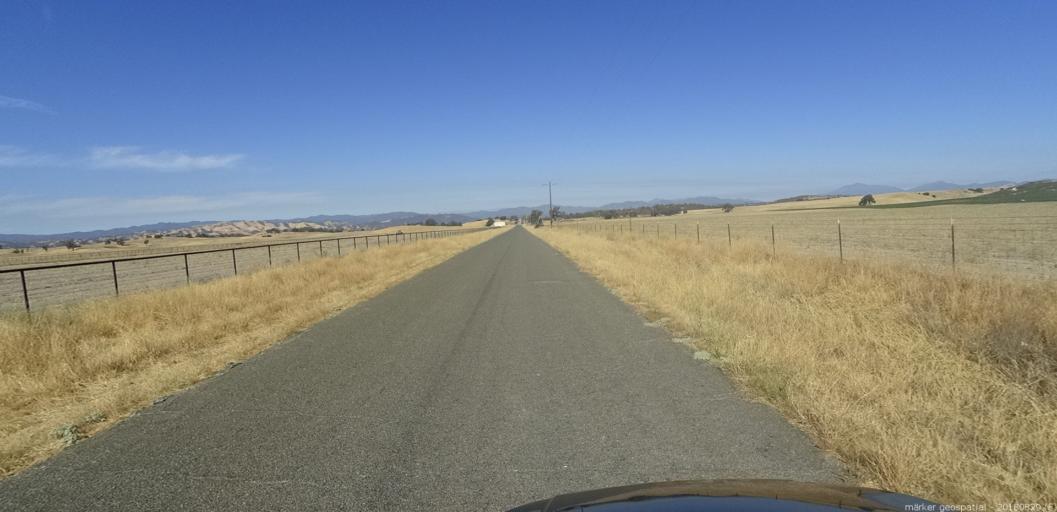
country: US
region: California
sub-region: Monterey County
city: King City
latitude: 35.9662
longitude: -121.1088
